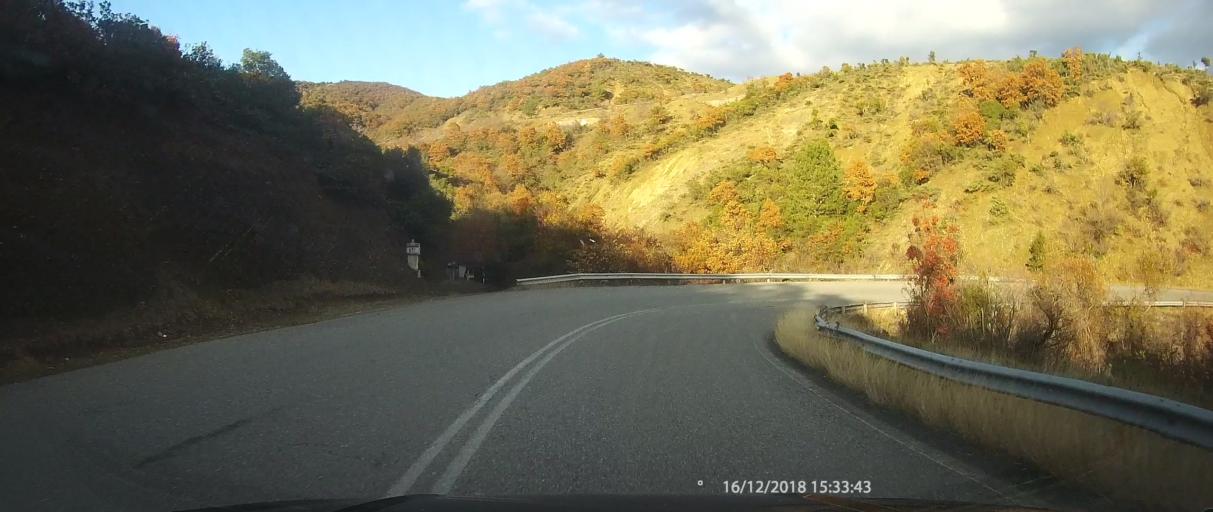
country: GR
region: Epirus
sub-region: Nomos Ioanninon
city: Konitsa
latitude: 40.0640
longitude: 20.7373
